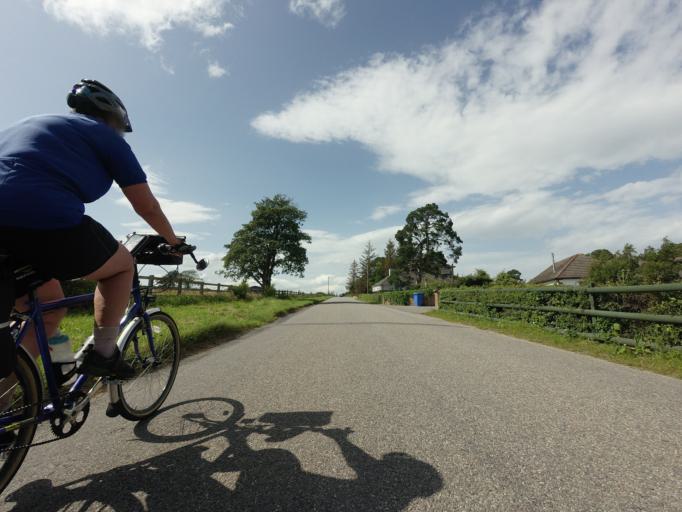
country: GB
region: Scotland
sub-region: Highland
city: Fortrose
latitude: 57.4869
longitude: -4.0993
